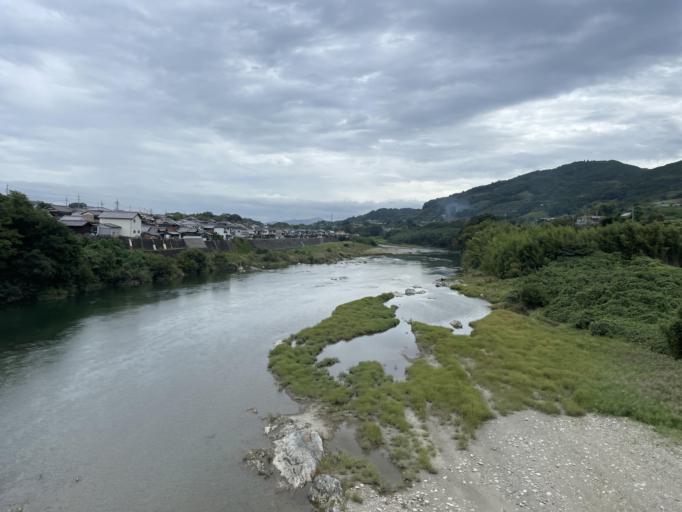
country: JP
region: Wakayama
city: Hashimoto
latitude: 34.3173
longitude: 135.6225
